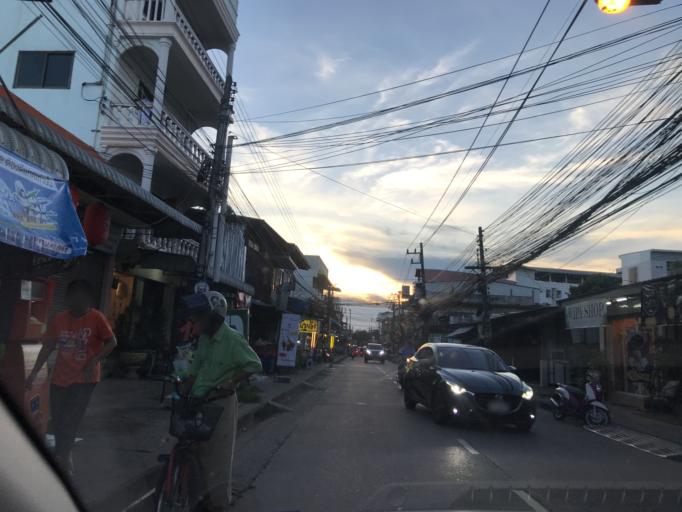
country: TH
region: Changwat Udon Thani
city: Udon Thani
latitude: 17.3945
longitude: 102.7930
